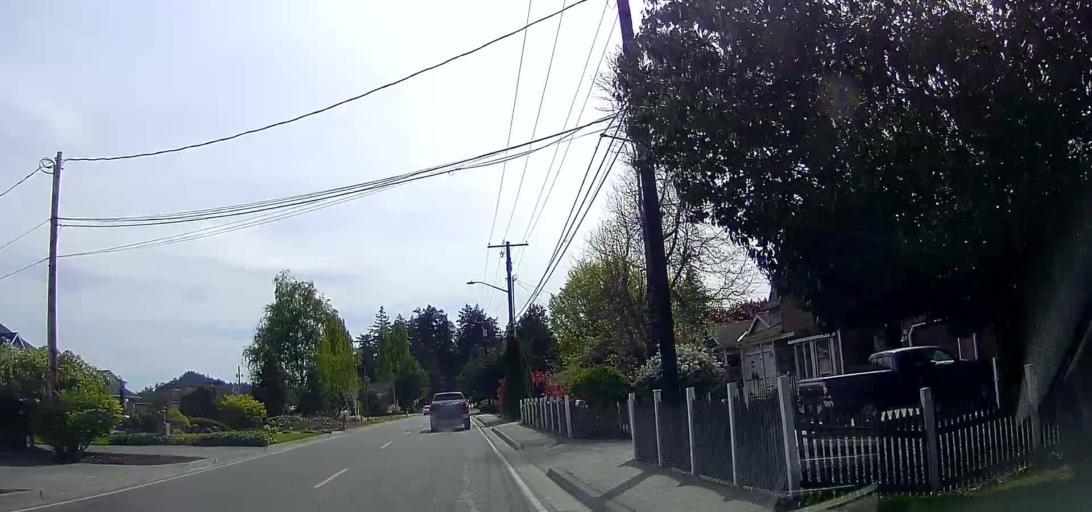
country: US
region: Washington
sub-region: Skagit County
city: Mount Vernon
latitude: 48.3868
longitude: -122.4938
